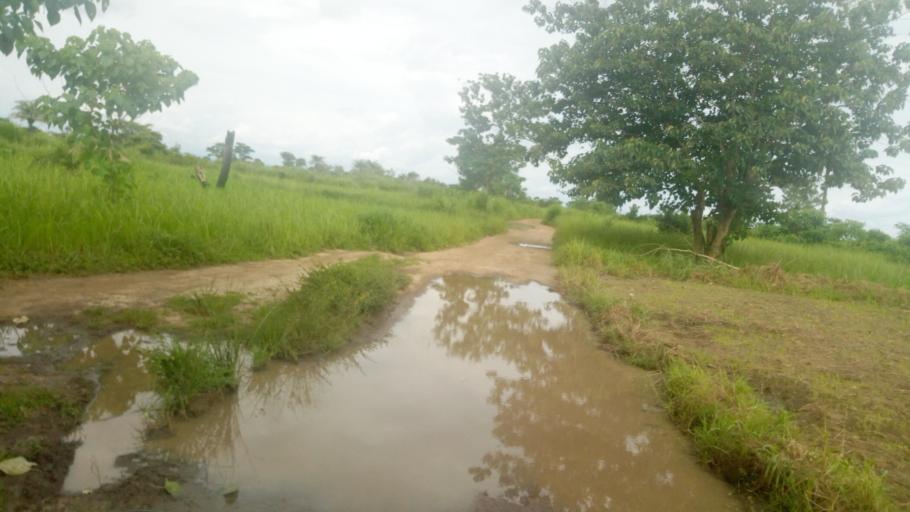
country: SL
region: Northern Province
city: Magburaka
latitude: 8.6731
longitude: -12.0320
